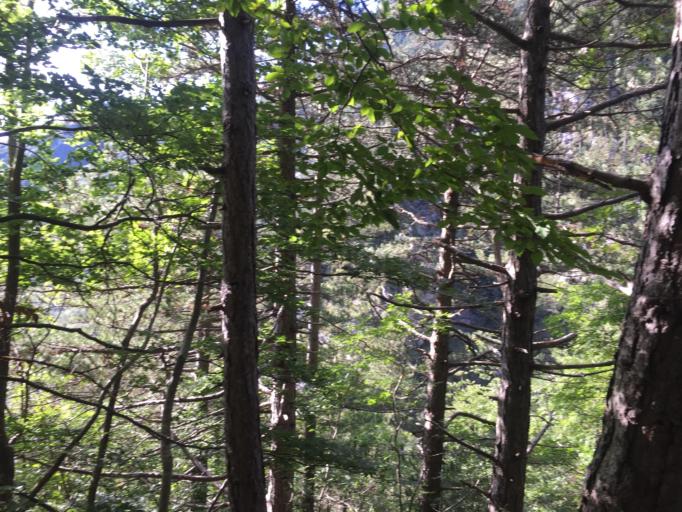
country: IT
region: Friuli Venezia Giulia
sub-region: Provincia di Udine
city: Dogna
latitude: 46.4329
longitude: 13.2881
